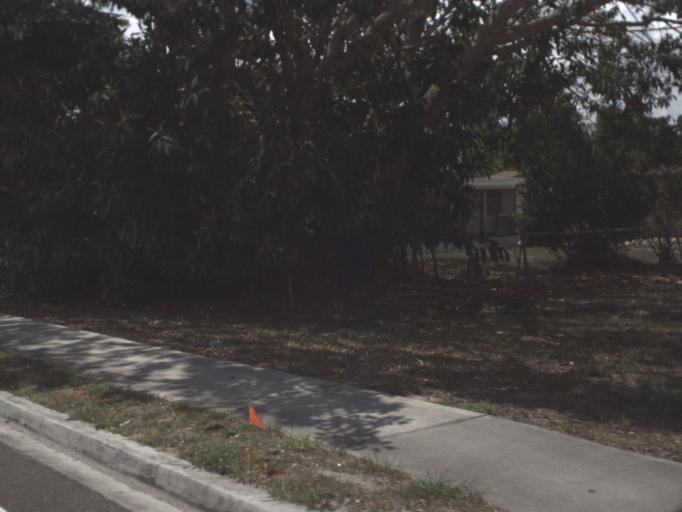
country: US
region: Florida
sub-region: Brevard County
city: Rockledge
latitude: 28.3451
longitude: -80.7426
